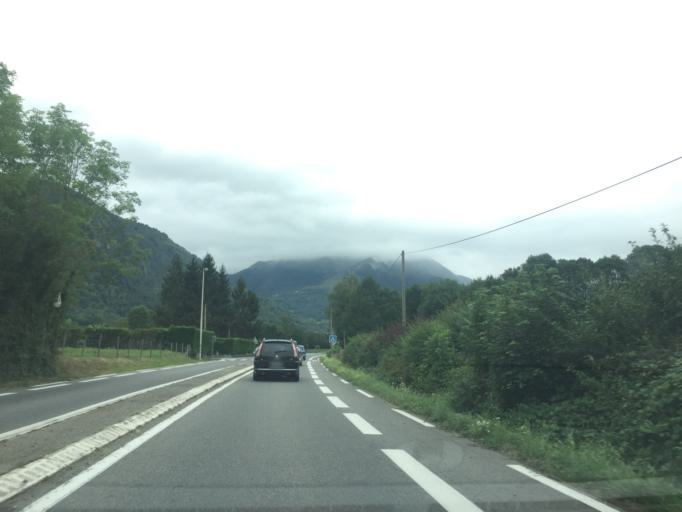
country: FR
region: Midi-Pyrenees
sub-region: Departement des Hautes-Pyrenees
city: Saint-Lary-Soulan
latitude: 42.8489
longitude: 0.3468
